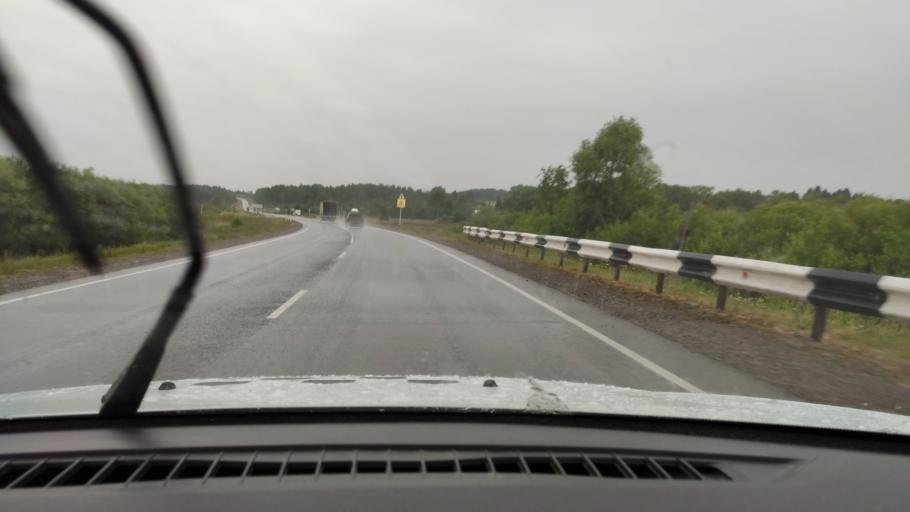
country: RU
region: Perm
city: Ocher
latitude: 57.5001
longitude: 54.5180
